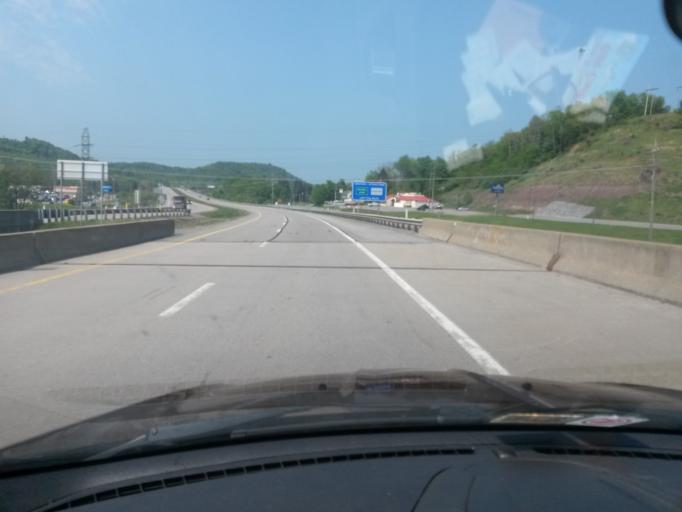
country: US
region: West Virginia
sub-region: Upshur County
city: Buckhannon
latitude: 39.0016
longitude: -80.2326
